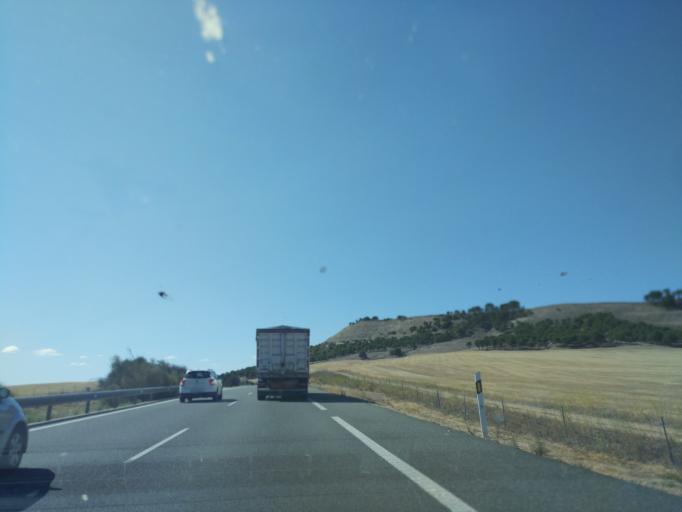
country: ES
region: Castille and Leon
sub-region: Provincia de Valladolid
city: Marzales
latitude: 41.6072
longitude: -5.1411
